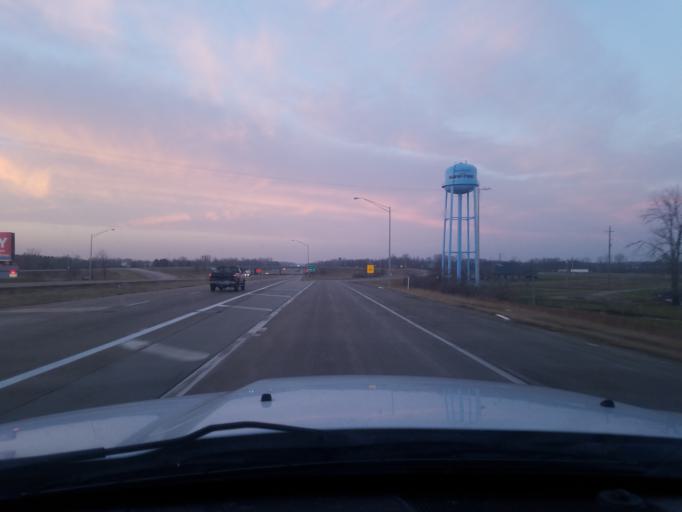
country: US
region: Indiana
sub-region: Huntington County
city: Markle
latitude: 40.8309
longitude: -85.3508
